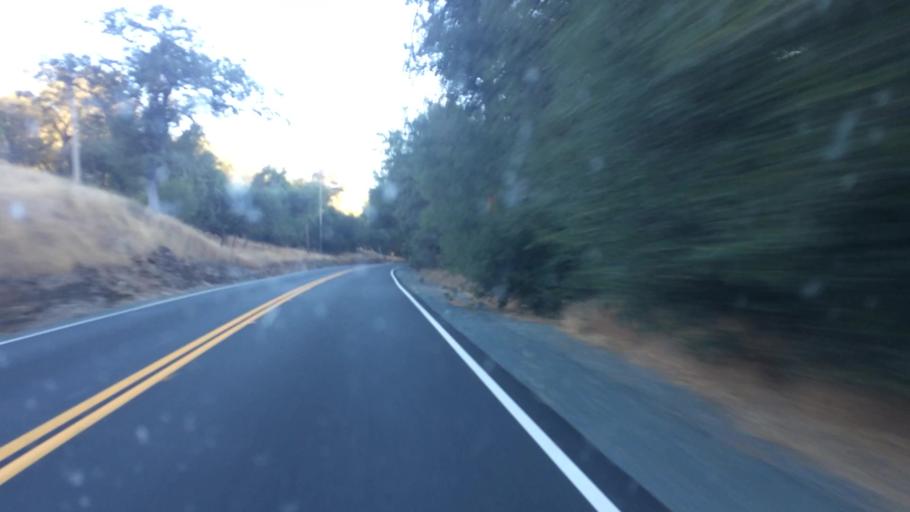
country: US
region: California
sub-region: Amador County
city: Plymouth
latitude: 38.5819
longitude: -120.8457
